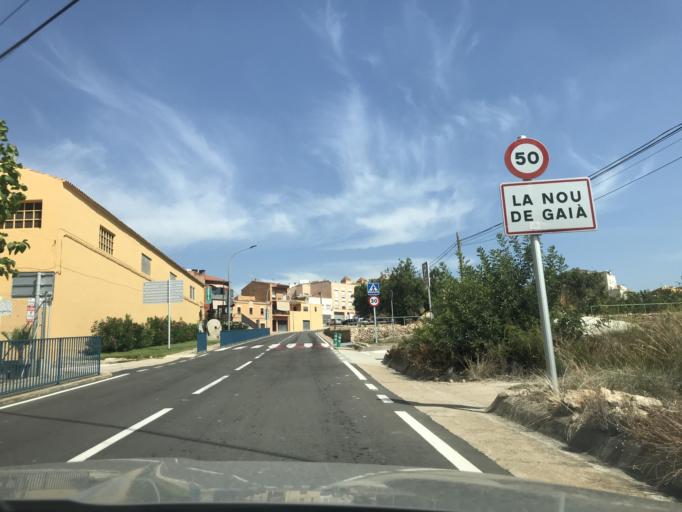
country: ES
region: Catalonia
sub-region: Provincia de Tarragona
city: Altafulla
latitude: 41.1799
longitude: 1.3730
